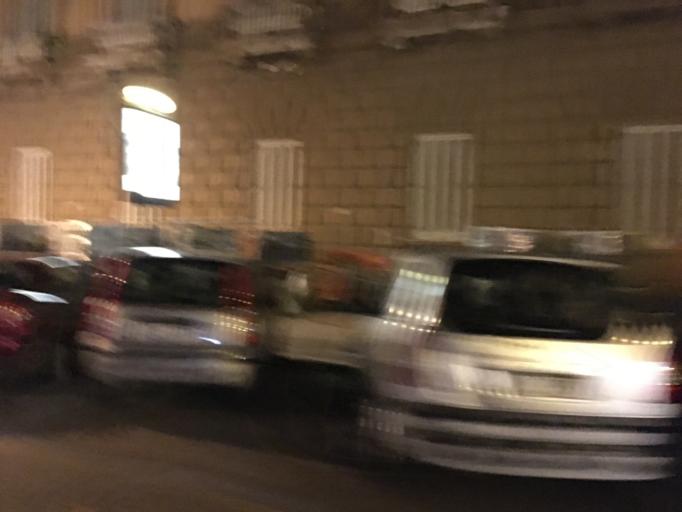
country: IT
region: Campania
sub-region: Provincia di Napoli
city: Napoli
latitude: 40.8337
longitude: 14.2331
